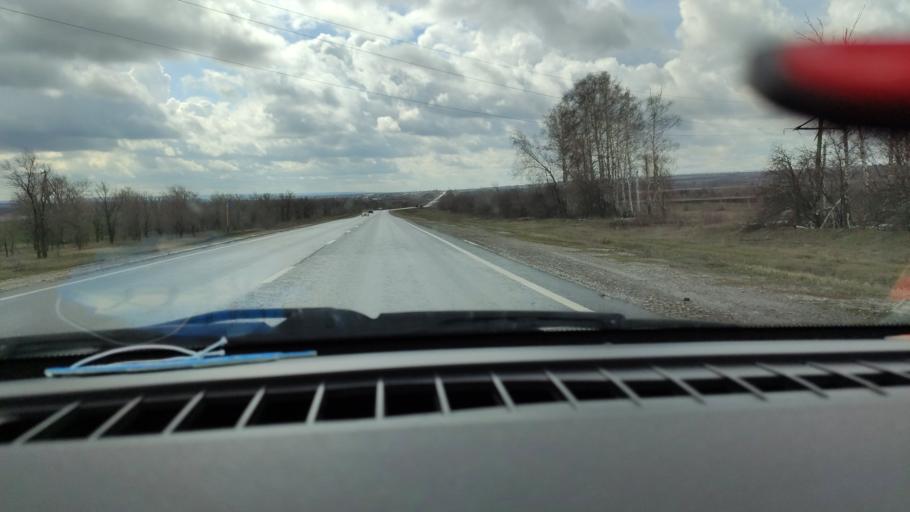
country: RU
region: Samara
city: Yelkhovka
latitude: 53.9031
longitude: 50.2680
